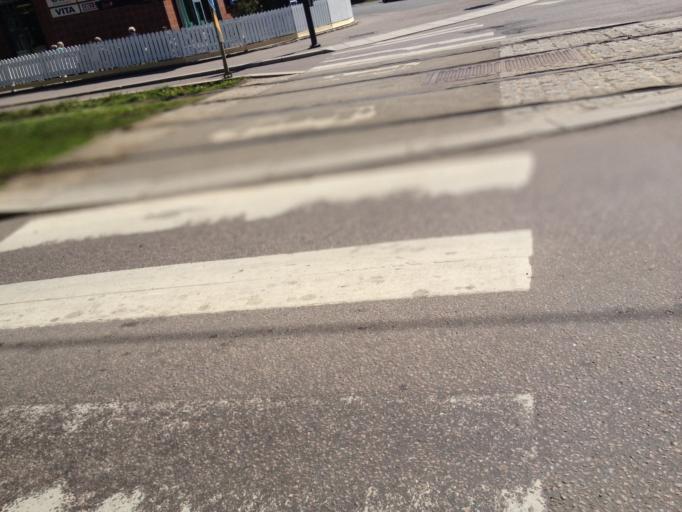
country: NO
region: Oslo
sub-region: Oslo
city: Oslo
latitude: 59.9374
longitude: 10.7672
